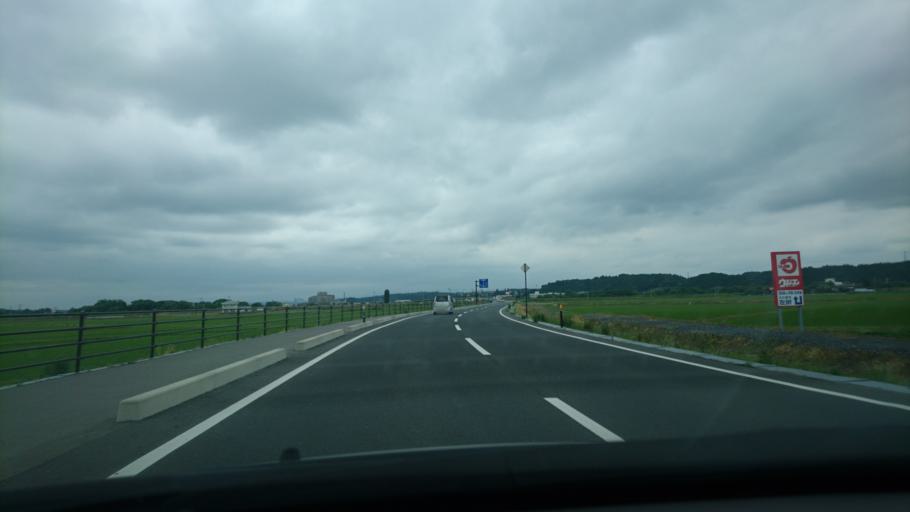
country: JP
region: Miyagi
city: Furukawa
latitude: 38.7467
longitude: 141.0329
